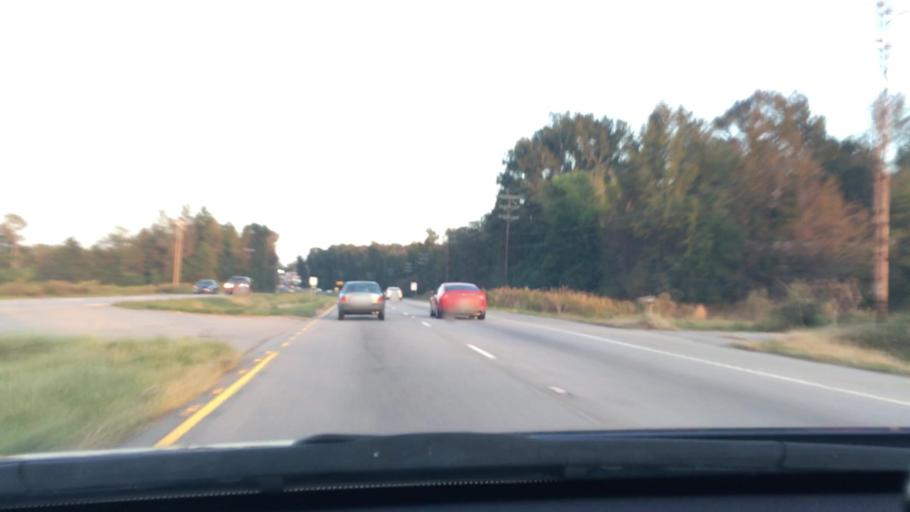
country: US
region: South Carolina
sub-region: Richland County
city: Hopkins
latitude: 33.9444
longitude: -80.8803
